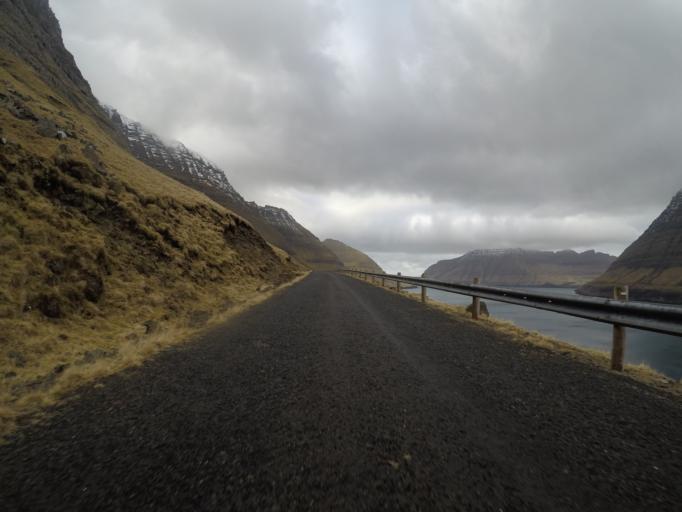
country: FO
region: Nordoyar
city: Klaksvik
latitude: 62.3279
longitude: -6.5687
